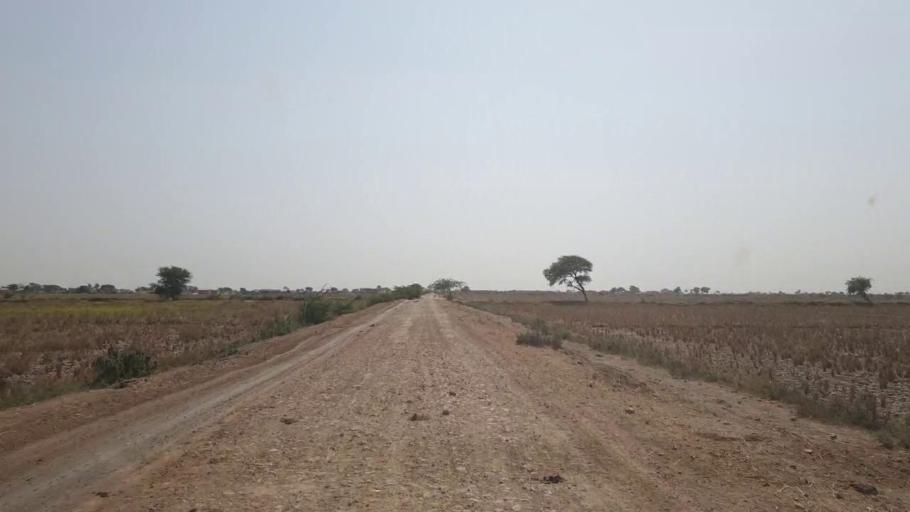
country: PK
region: Sindh
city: Jati
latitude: 24.4321
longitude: 68.5523
